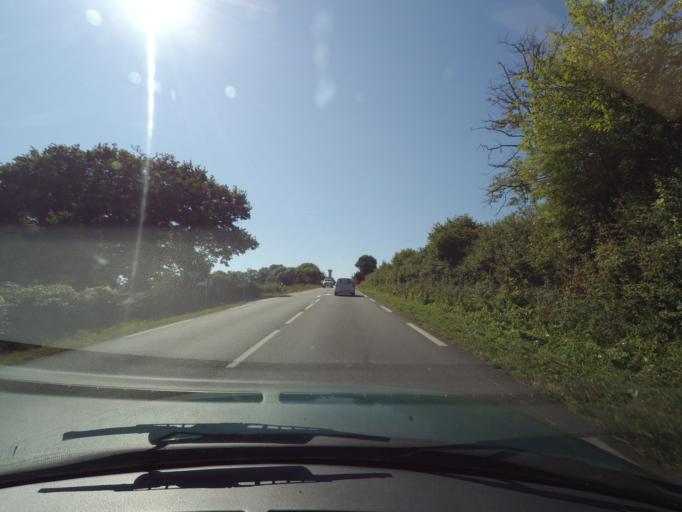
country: FR
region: Limousin
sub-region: Departement de la Haute-Vienne
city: Peyrat-de-Bellac
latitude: 46.1532
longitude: 0.9629
